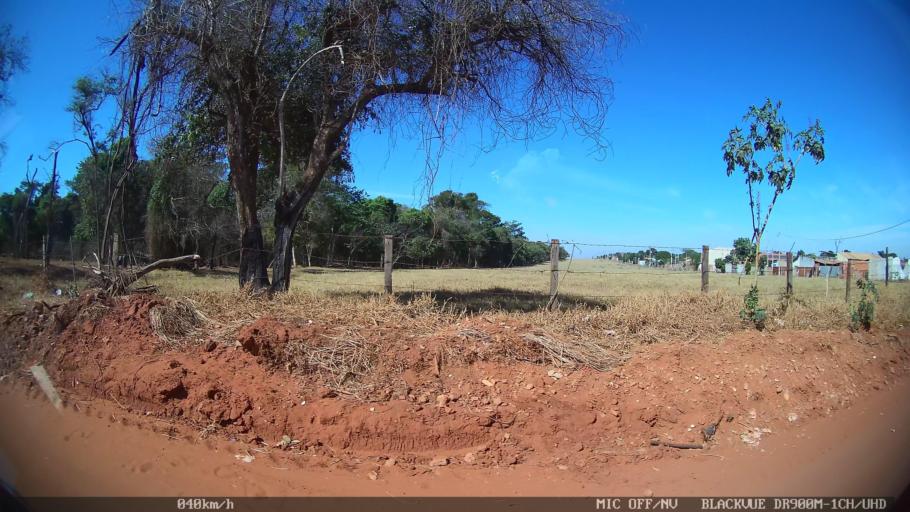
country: BR
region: Sao Paulo
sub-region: Sao Jose Do Rio Preto
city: Sao Jose do Rio Preto
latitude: -20.7429
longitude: -49.4307
